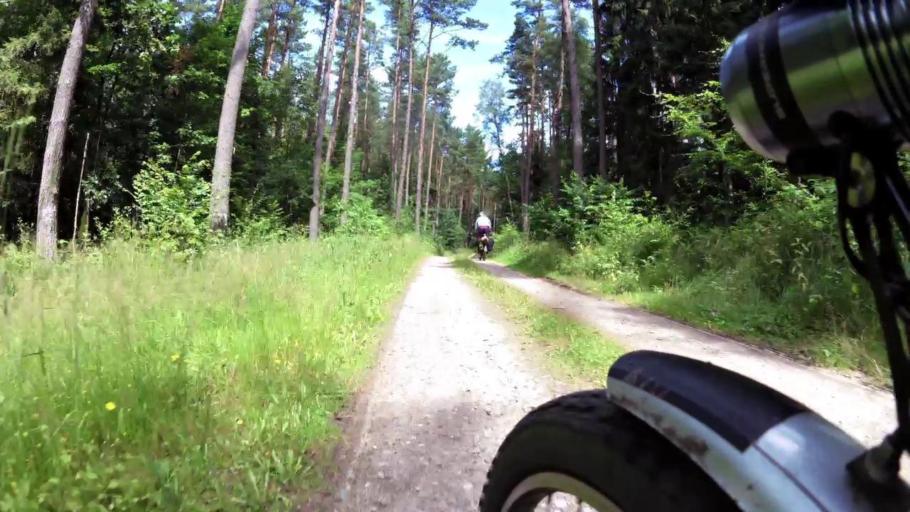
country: PL
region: West Pomeranian Voivodeship
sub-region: Powiat swidwinski
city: Rabino
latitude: 53.8851
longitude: 15.9785
